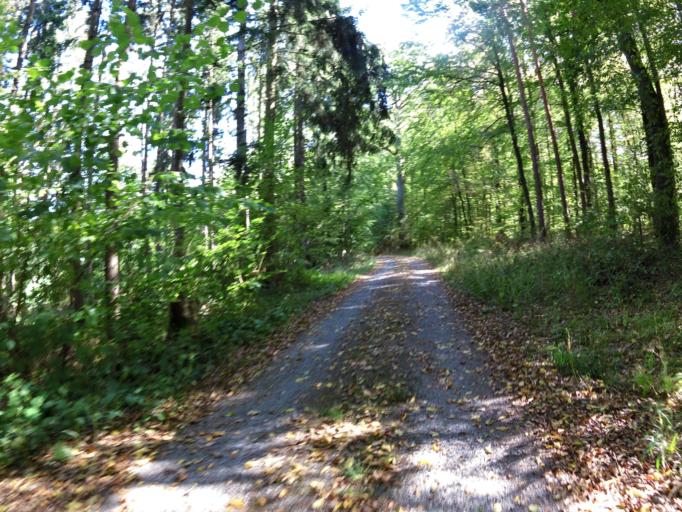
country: DE
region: Bavaria
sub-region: Regierungsbezirk Unterfranken
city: Eisingen
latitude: 49.7728
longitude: 9.8288
